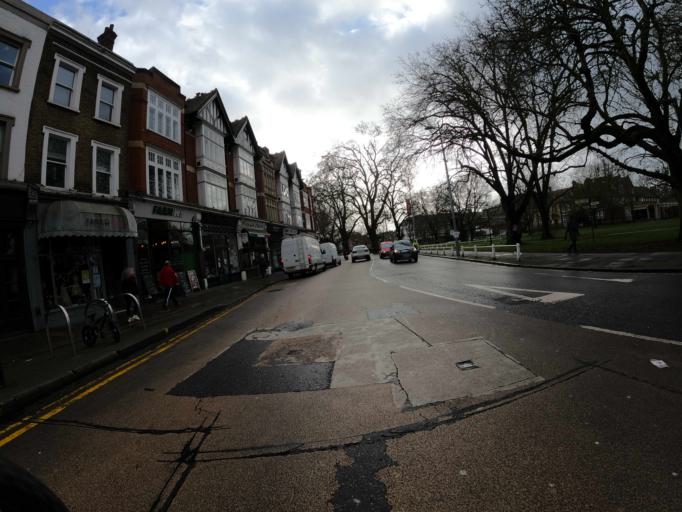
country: GB
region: England
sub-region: Greater London
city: Ealing
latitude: 51.5110
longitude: -0.3054
